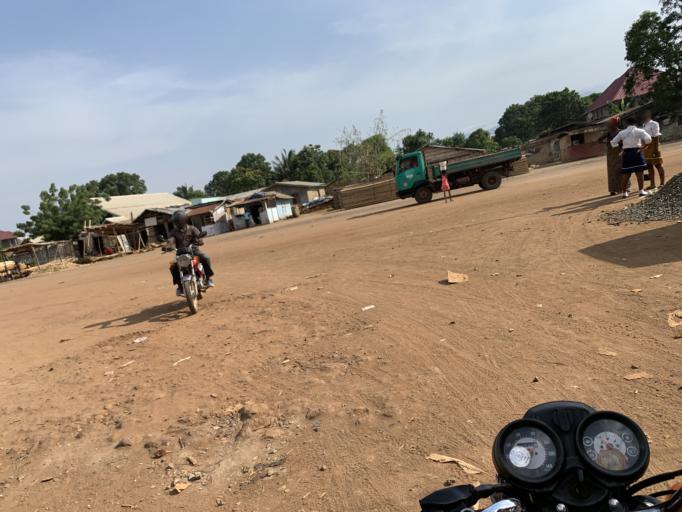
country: SL
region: Western Area
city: Waterloo
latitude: 8.3370
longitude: -13.0427
